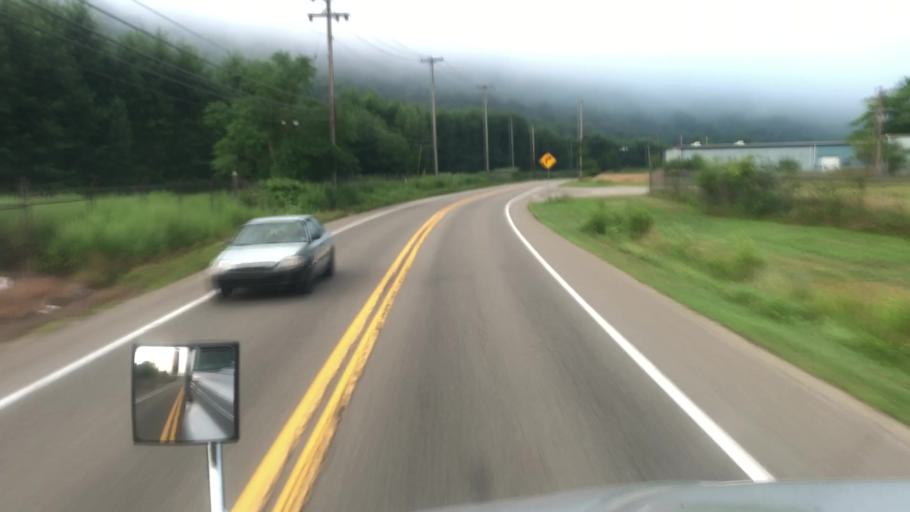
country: US
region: Pennsylvania
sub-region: Venango County
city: Hasson Heights
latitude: 41.4504
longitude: -79.6895
